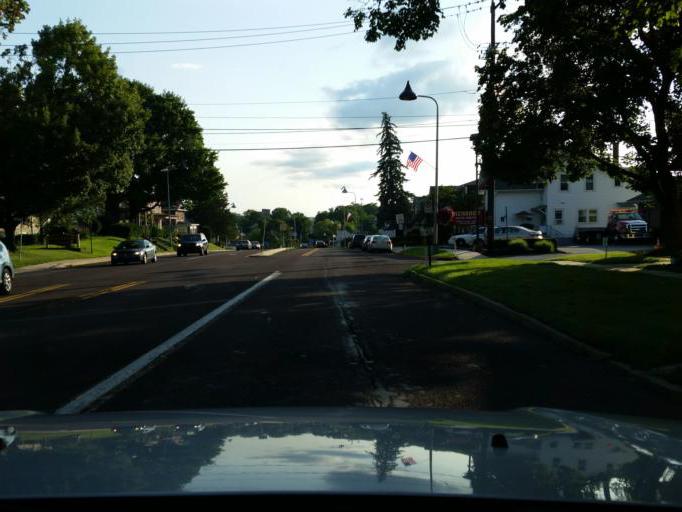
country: US
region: Pennsylvania
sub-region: Dauphin County
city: Hershey
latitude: 40.2822
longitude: -76.6596
